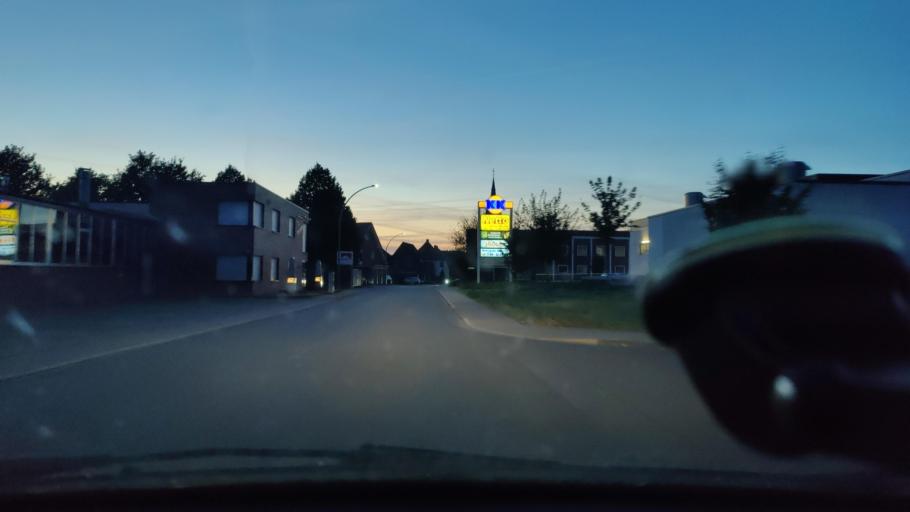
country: DE
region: North Rhine-Westphalia
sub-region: Regierungsbezirk Munster
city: Sudlohn
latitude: 51.9072
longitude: 6.8622
